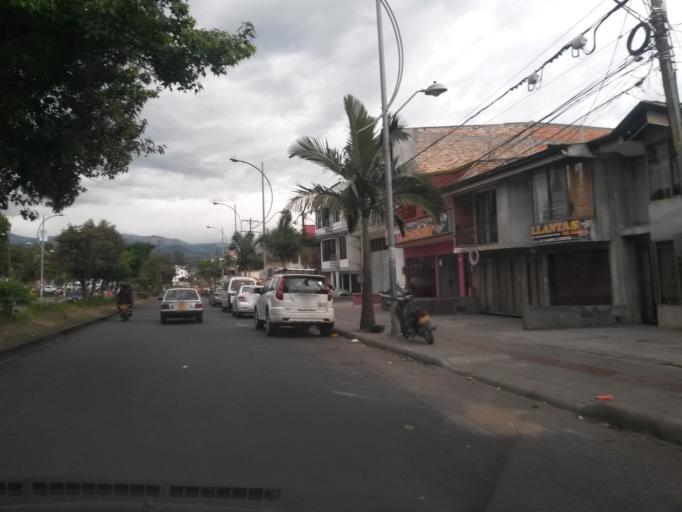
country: CO
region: Cauca
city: Popayan
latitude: 2.4511
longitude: -76.6097
